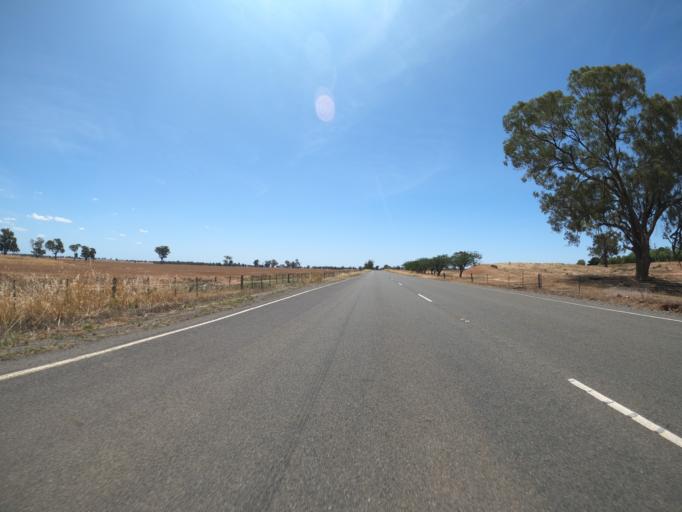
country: AU
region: Victoria
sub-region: Moira
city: Yarrawonga
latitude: -36.1562
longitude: 145.9672
